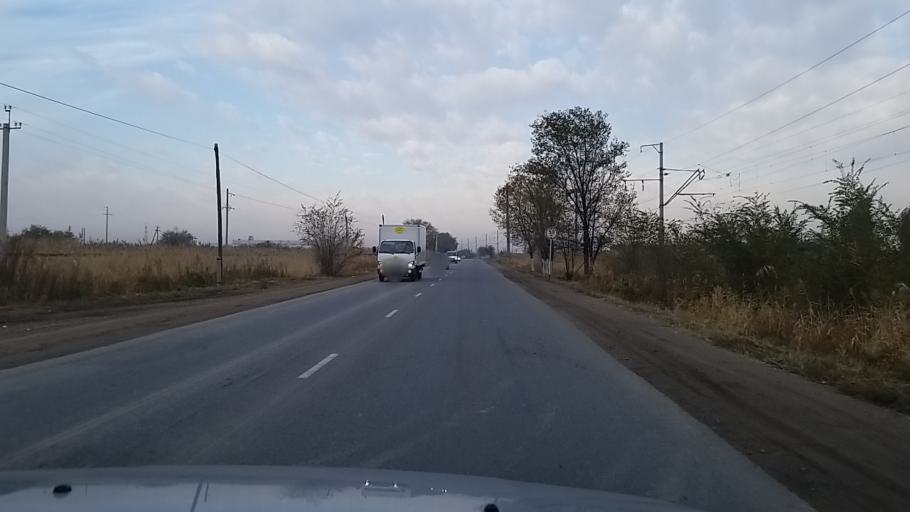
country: KZ
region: Almaty Oblysy
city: Burunday
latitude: 43.3569
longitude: 76.7903
